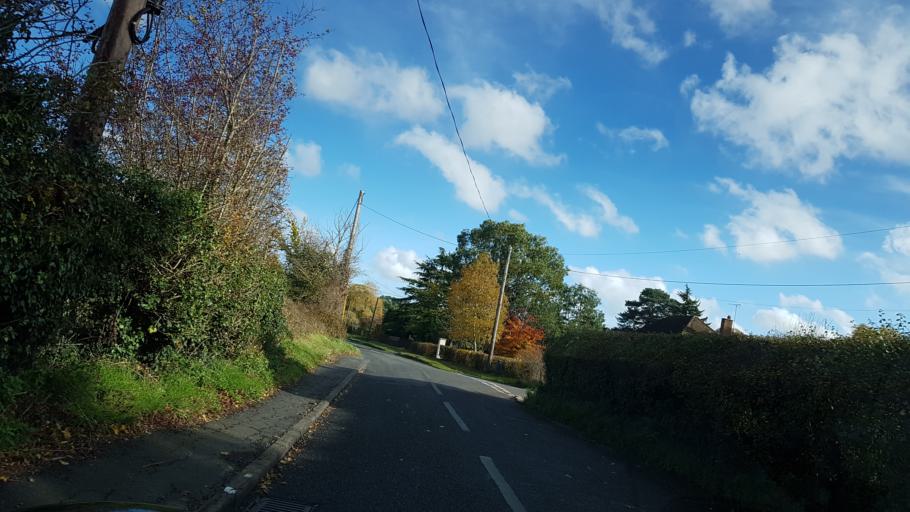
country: GB
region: England
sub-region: Surrey
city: Seale
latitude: 51.2209
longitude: -0.7430
